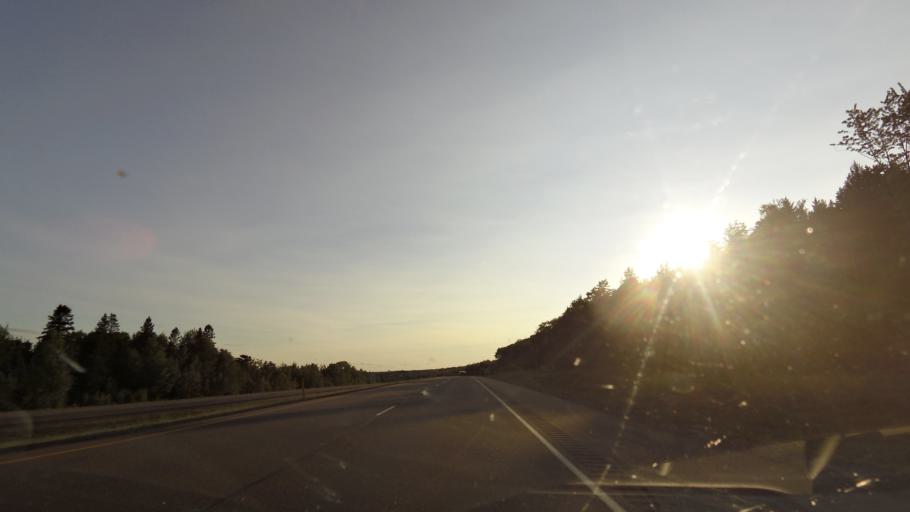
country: CA
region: New Brunswick
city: Moncton
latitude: 46.1275
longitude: -64.9079
